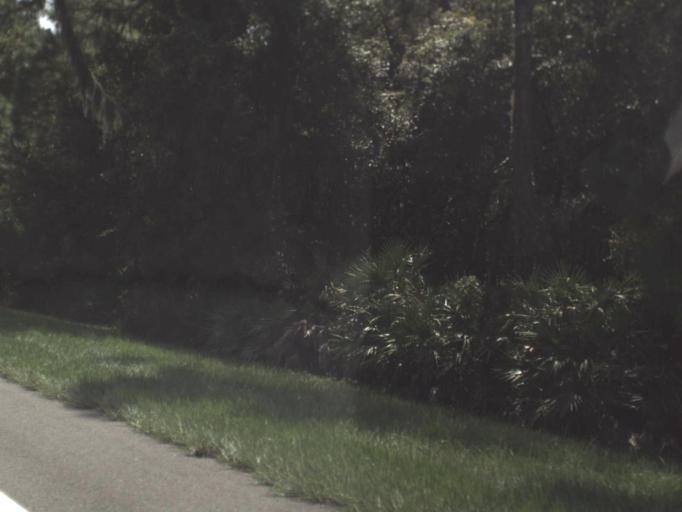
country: US
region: Florida
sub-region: Sarasota County
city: The Meadows
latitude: 27.4014
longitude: -82.3099
